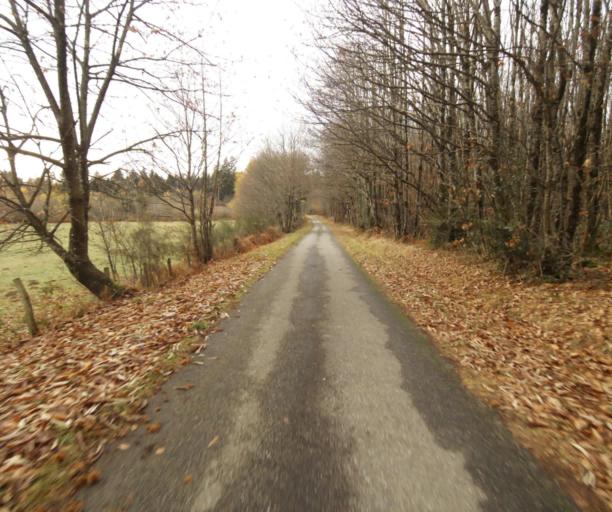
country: FR
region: Limousin
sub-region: Departement de la Correze
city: Sainte-Fortunade
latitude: 45.1934
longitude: 1.7622
